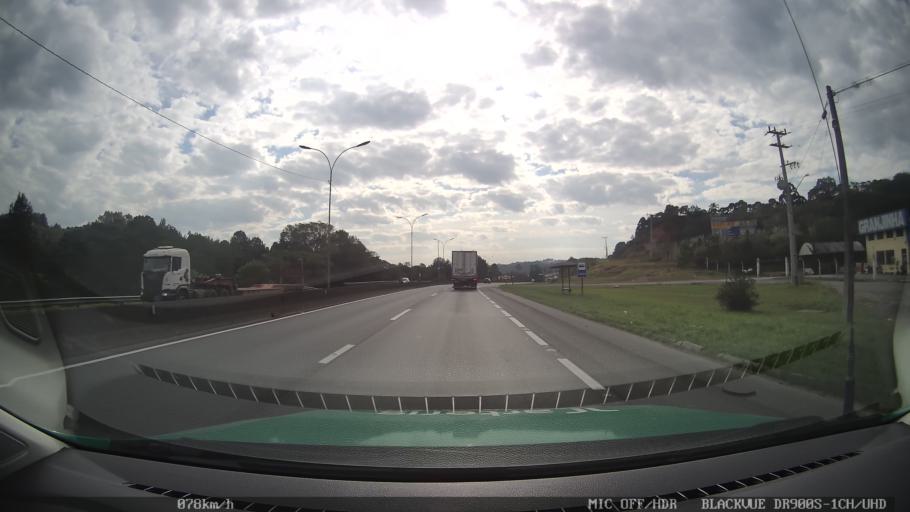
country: BR
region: Parana
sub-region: Campina Grande Do Sul
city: Campina Grande do Sul
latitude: -25.3214
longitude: -49.0246
